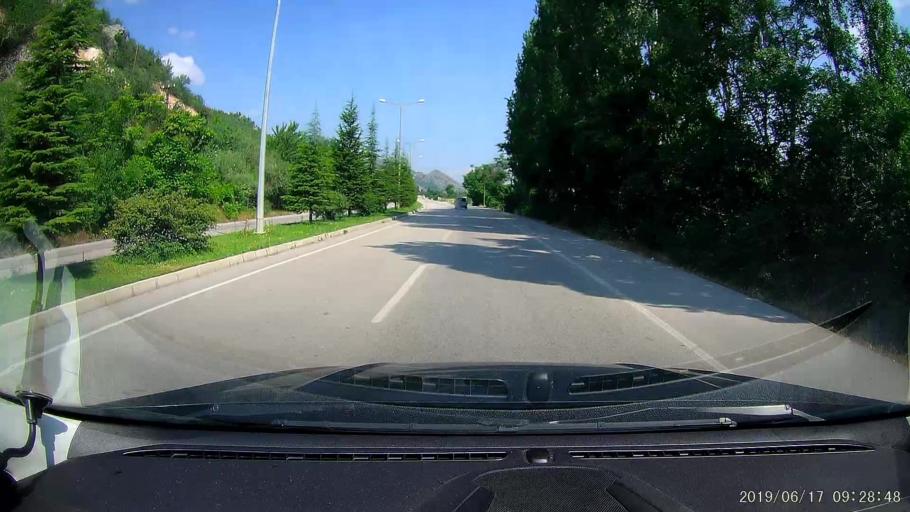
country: TR
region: Amasya
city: Amasya
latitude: 40.6922
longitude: 35.8201
